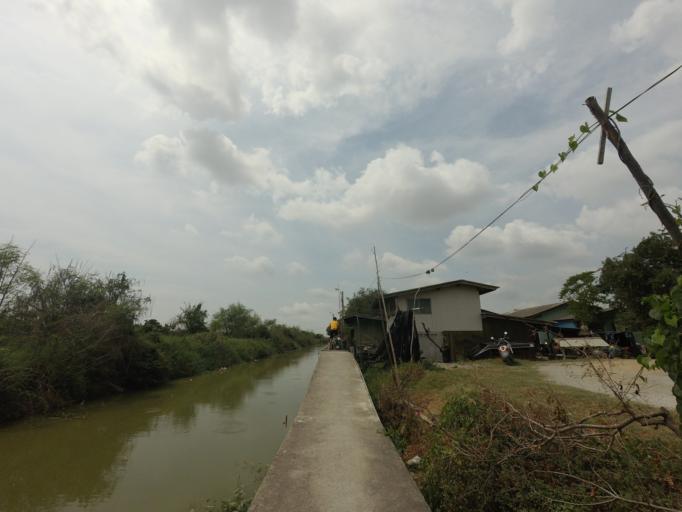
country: TH
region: Bangkok
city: Lat Krabang
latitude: 13.6815
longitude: 100.7698
